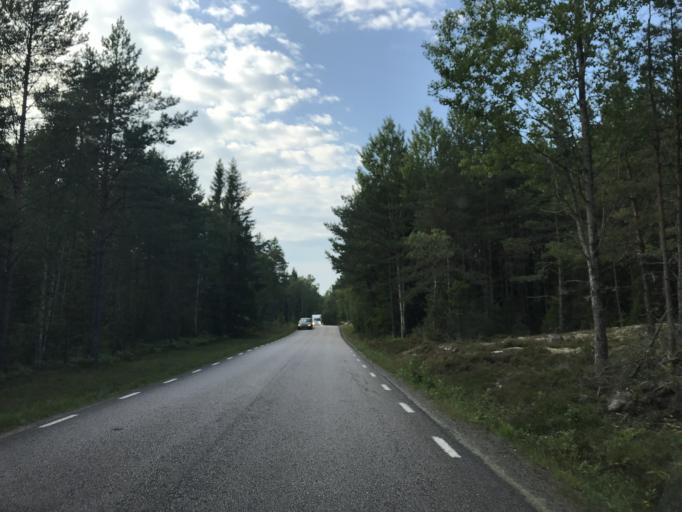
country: SE
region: Stockholm
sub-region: Norrtalje Kommun
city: Bjorko
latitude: 59.8861
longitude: 18.9792
